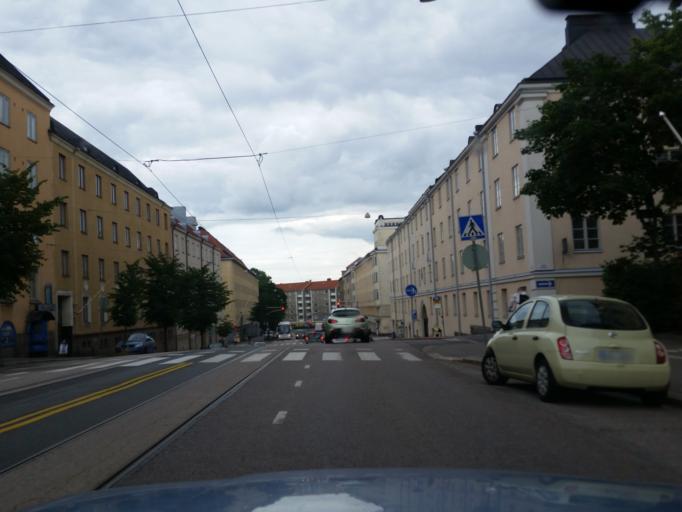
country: FI
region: Uusimaa
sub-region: Helsinki
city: Helsinki
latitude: 60.1950
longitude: 24.9582
